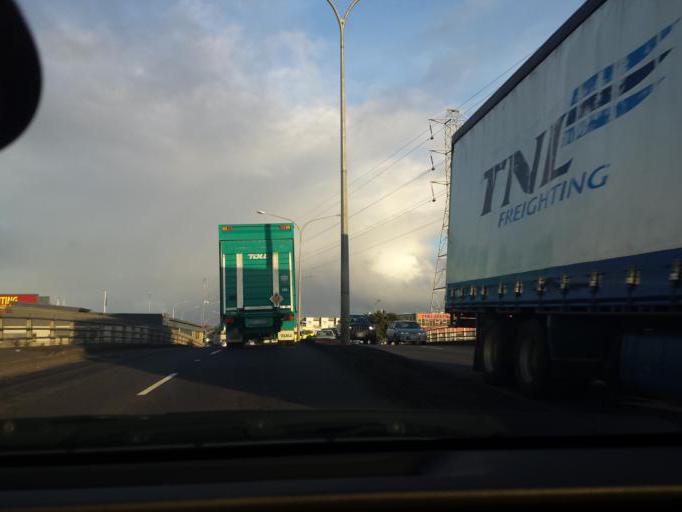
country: NZ
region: Auckland
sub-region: Auckland
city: Mangere
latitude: -36.9266
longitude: 174.7871
